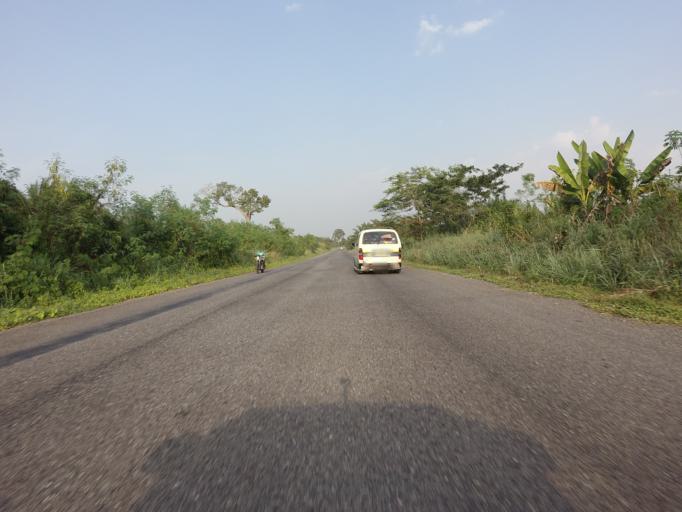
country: GH
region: Volta
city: Ho
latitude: 6.4373
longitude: 0.1943
